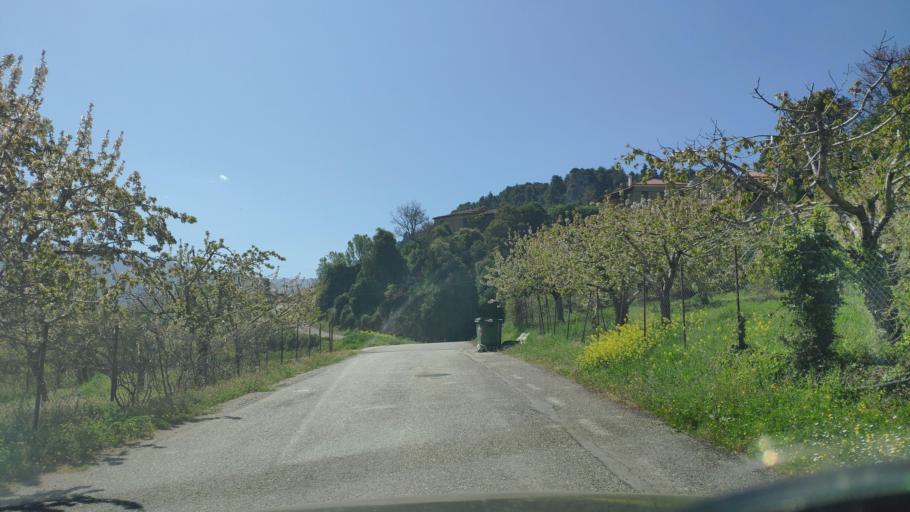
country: GR
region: West Greece
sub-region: Nomos Achaias
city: Akrata
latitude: 38.0992
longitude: 22.3189
